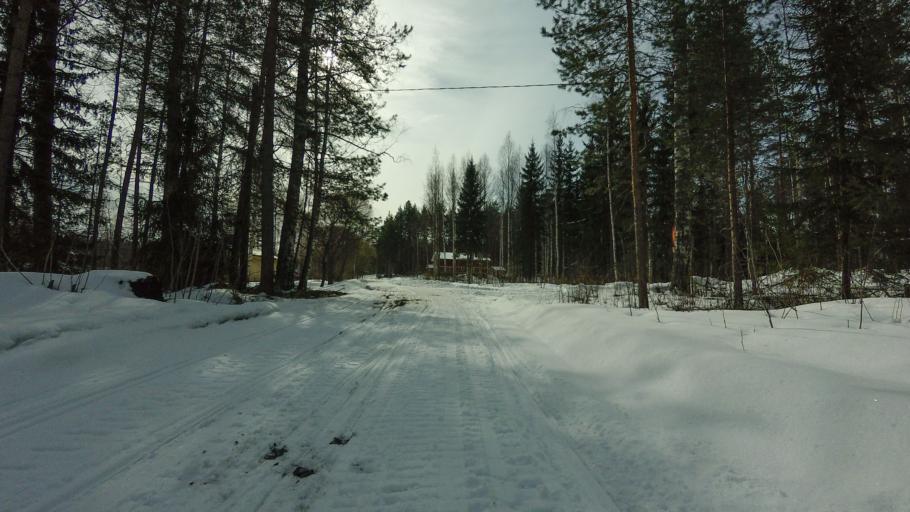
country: FI
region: Southern Savonia
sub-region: Savonlinna
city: Rantasalmi
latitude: 62.1198
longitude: 28.6029
